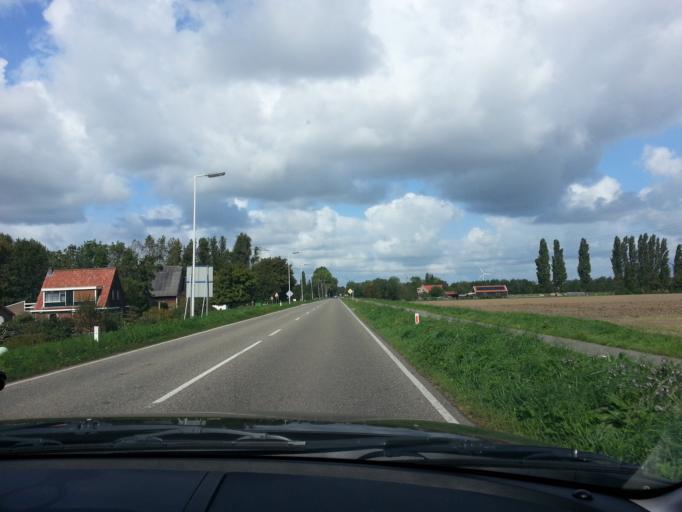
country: NL
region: South Holland
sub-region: Gemeente Spijkenisse
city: Spijkenisse
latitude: 51.8383
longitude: 4.2500
